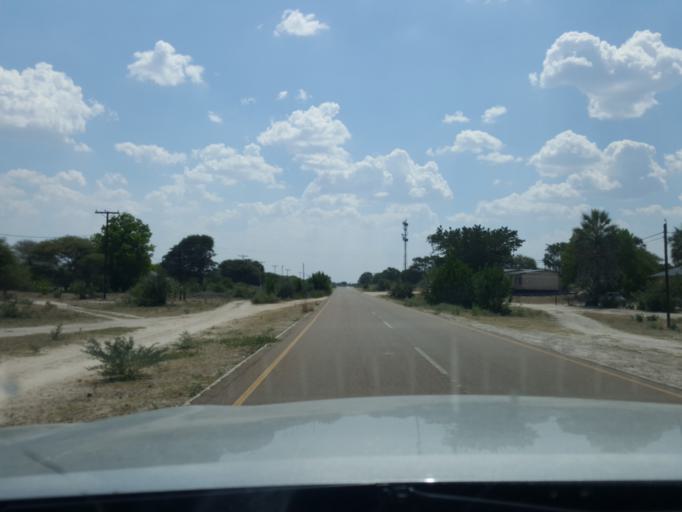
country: BW
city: Nokaneng
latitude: -19.6639
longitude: 22.1901
